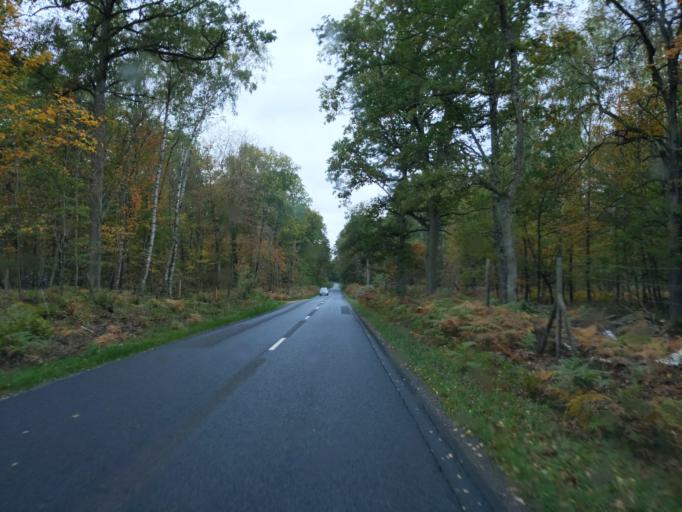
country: FR
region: Ile-de-France
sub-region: Departement des Yvelines
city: Saint-Arnoult-en-Yvelines
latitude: 48.6009
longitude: 1.9430
